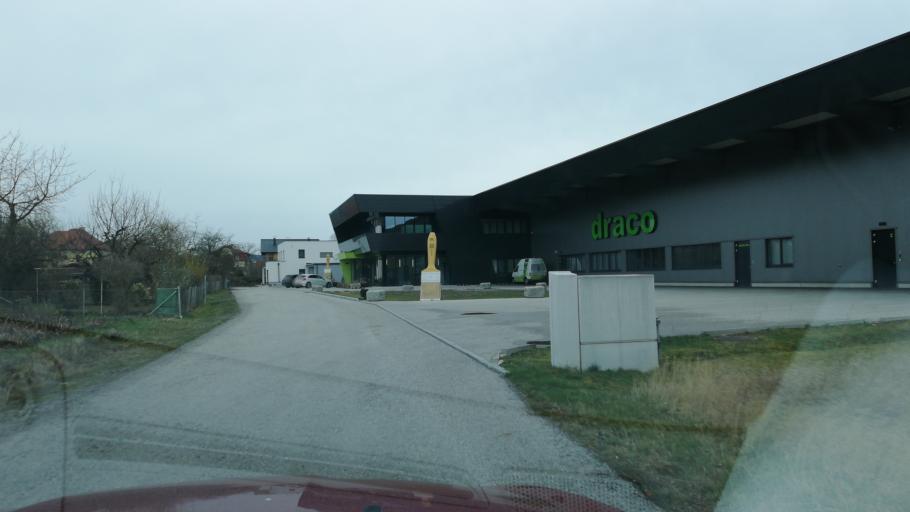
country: AT
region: Upper Austria
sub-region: Politischer Bezirk Urfahr-Umgebung
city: Feldkirchen an der Donau
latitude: 48.3024
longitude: 14.0186
